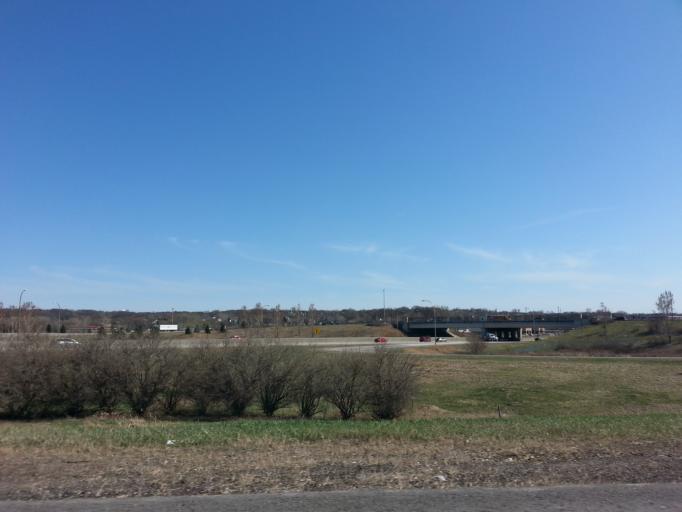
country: US
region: Minnesota
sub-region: Dakota County
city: Burnsville
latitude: 44.7166
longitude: -93.2841
